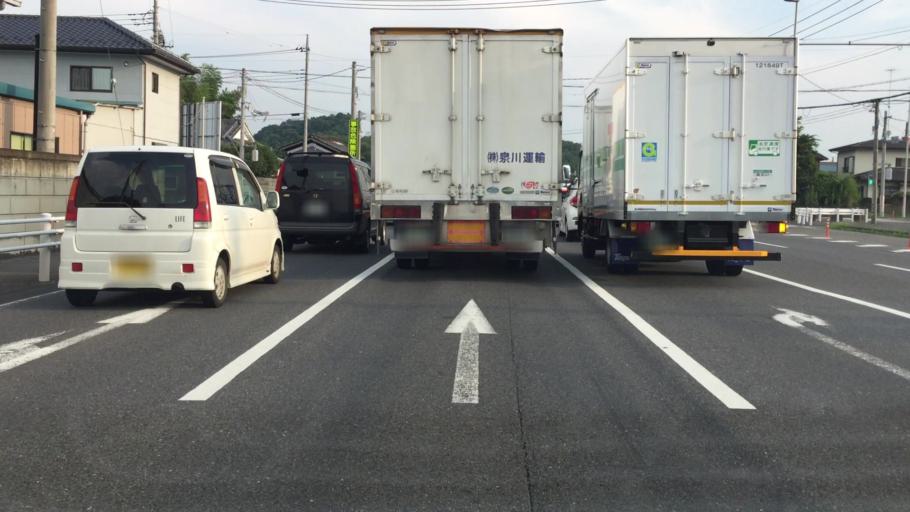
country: JP
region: Tochigi
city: Fujioka
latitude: 36.3194
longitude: 139.6766
